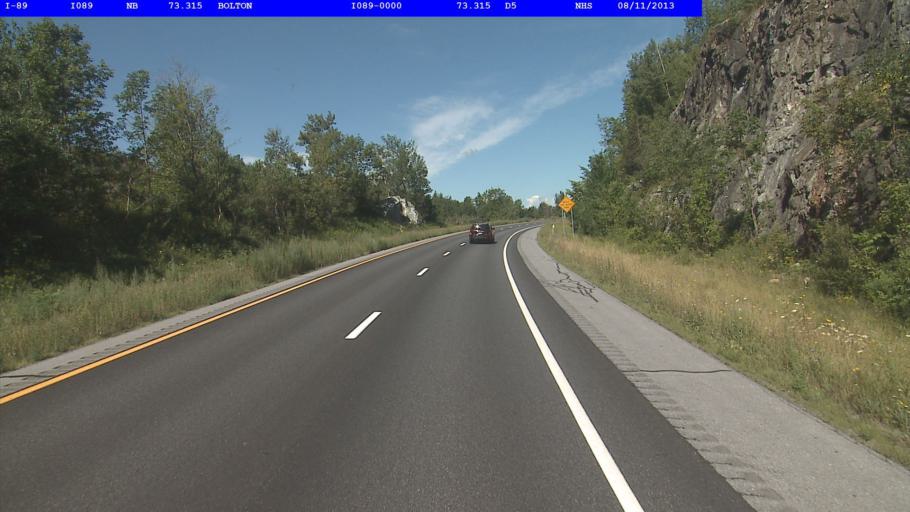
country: US
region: Vermont
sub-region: Chittenden County
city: Jericho
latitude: 44.3836
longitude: -72.9315
